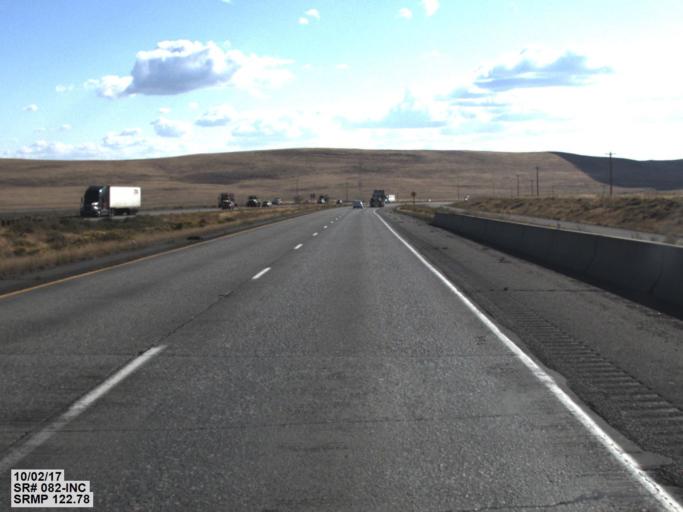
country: US
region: Washington
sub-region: Benton County
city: Highland
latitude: 46.0248
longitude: -119.2251
